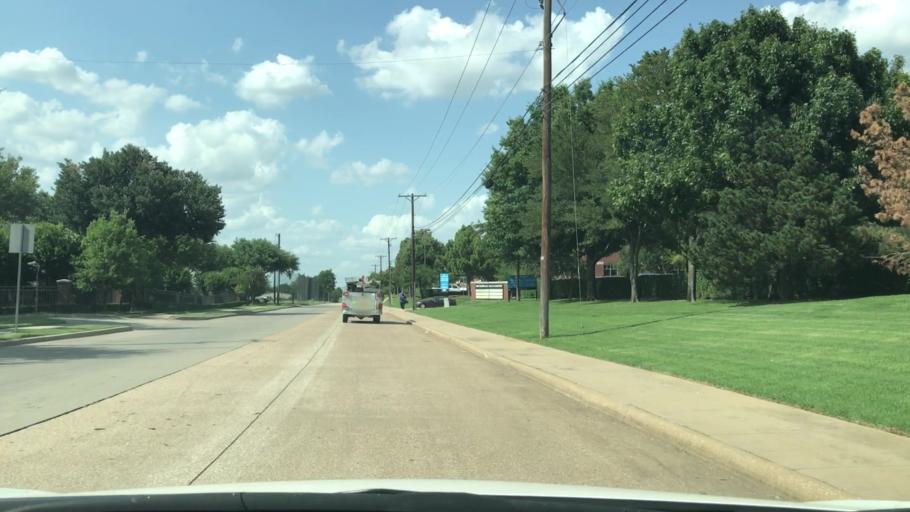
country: US
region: Texas
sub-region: Dallas County
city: Addison
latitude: 32.9731
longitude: -96.8514
